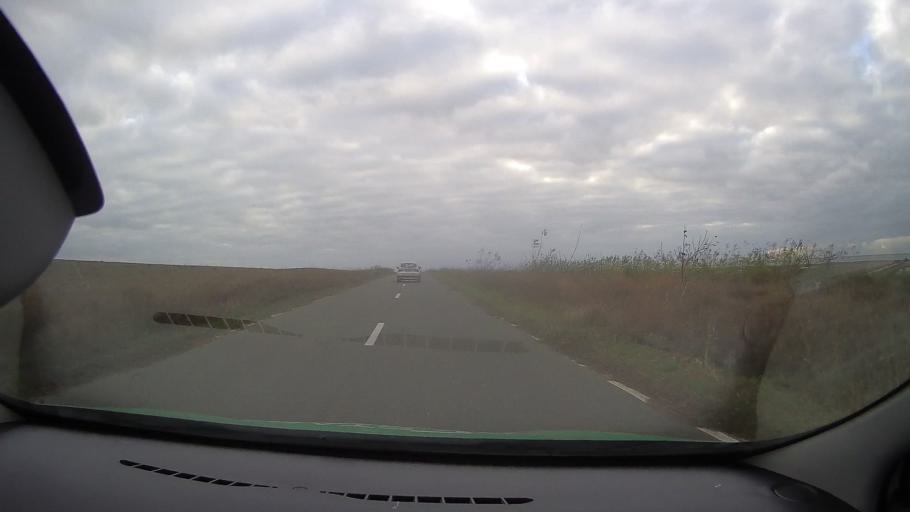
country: RO
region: Tulcea
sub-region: Comuna Jurilovca
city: Jurilovca
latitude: 44.7615
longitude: 28.8978
